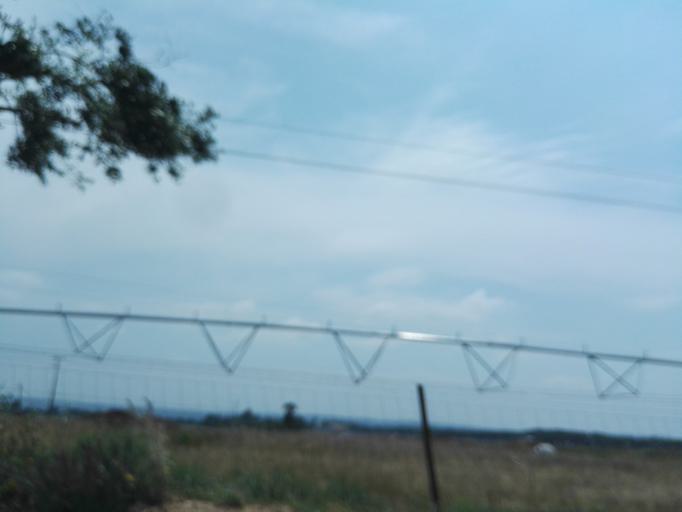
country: PT
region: Santarem
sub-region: Entroncamento
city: Entroncamento
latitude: 39.4523
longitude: -8.4635
